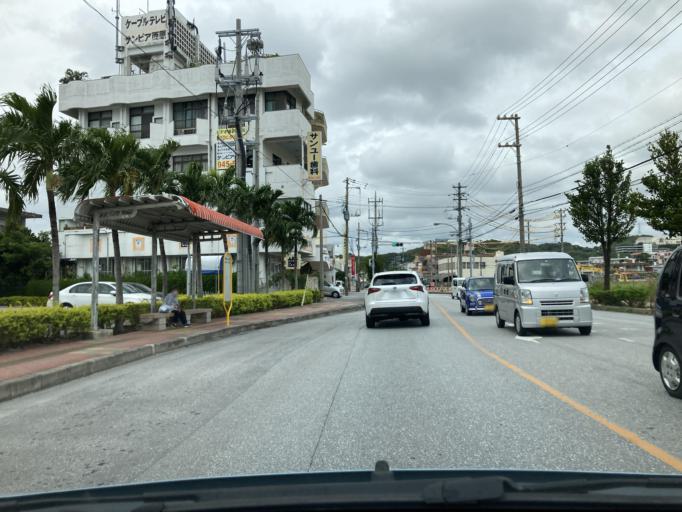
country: JP
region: Okinawa
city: Ginowan
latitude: 26.2256
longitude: 127.7653
